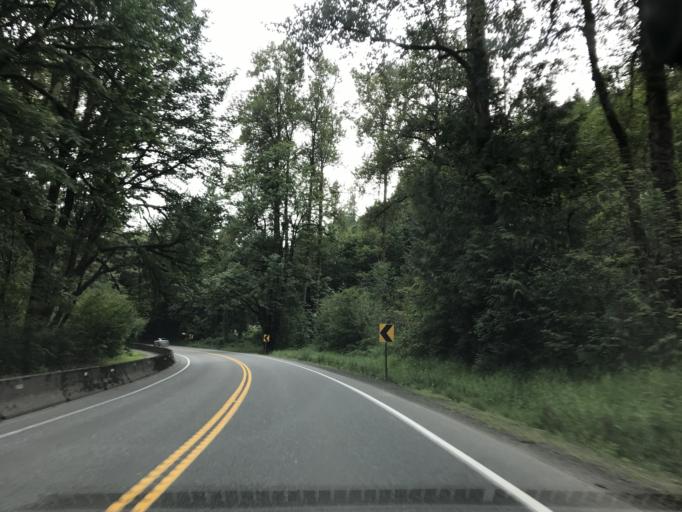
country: US
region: Washington
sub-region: King County
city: Fall City
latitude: 47.5411
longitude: -121.9083
